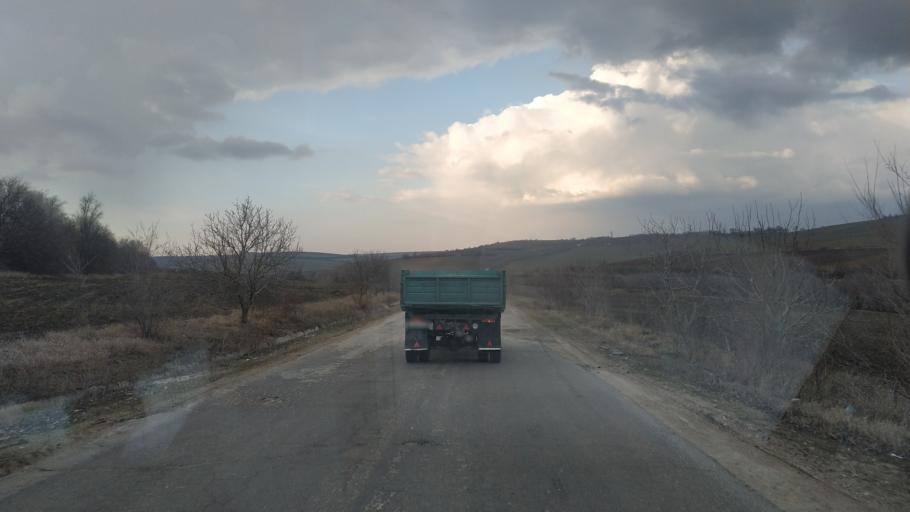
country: MD
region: Anenii Noi
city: Anenii Noi
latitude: 46.9428
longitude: 29.2839
